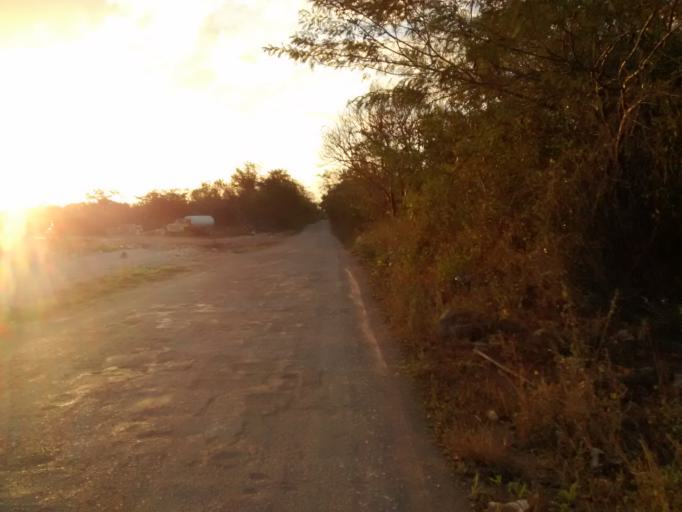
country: MX
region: Yucatan
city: Valladolid
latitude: 20.6835
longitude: -88.1741
